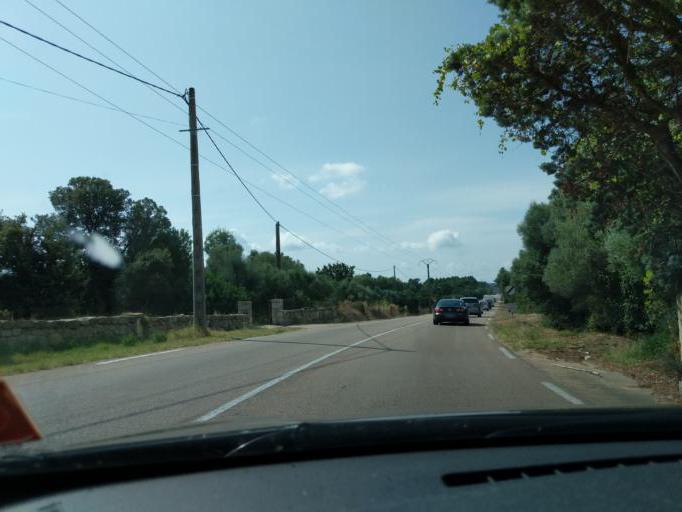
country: FR
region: Corsica
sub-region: Departement de la Corse-du-Sud
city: Porto-Vecchio
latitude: 41.6619
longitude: 9.3063
